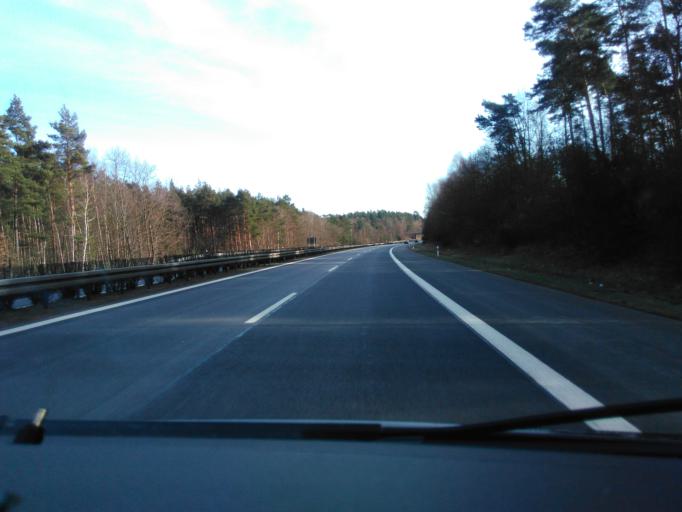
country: DE
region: Brandenburg
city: Bronkow
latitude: 51.6568
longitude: 13.9324
